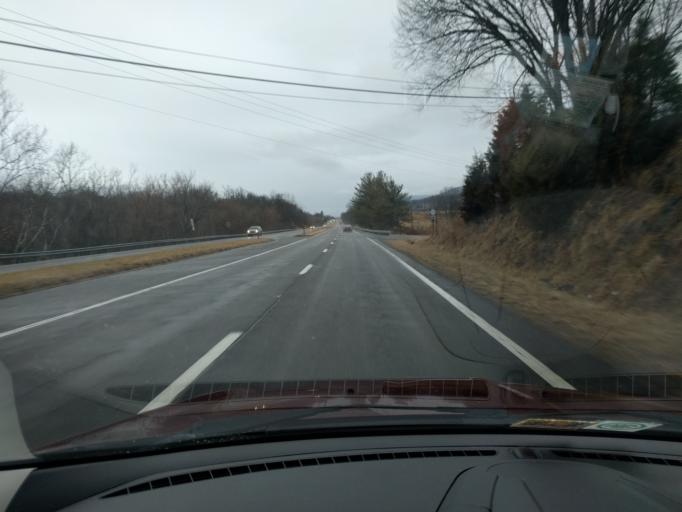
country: US
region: Virginia
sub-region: Giles County
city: Pembroke
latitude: 37.3053
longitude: -80.5727
